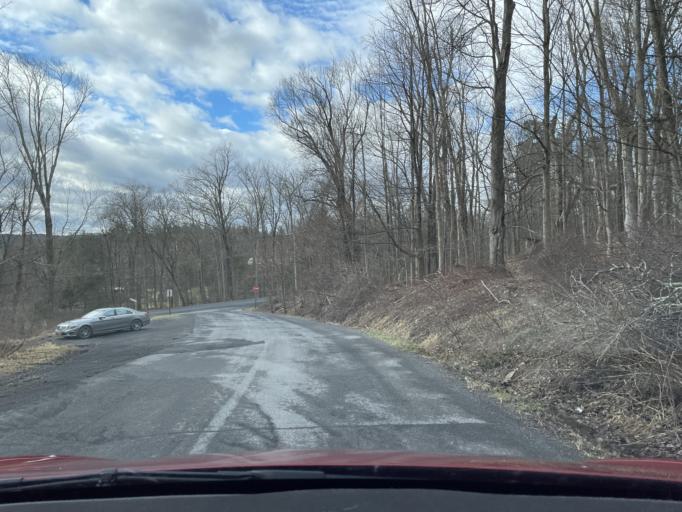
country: US
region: New York
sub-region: Ulster County
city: Woodstock
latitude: 42.0532
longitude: -74.1476
